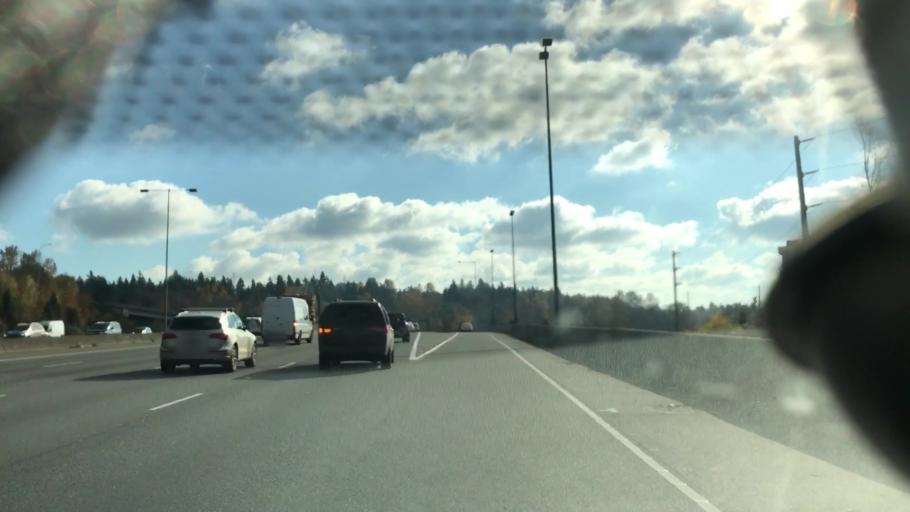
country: US
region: Washington
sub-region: King County
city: Bellevue
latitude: 47.6055
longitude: -122.1865
